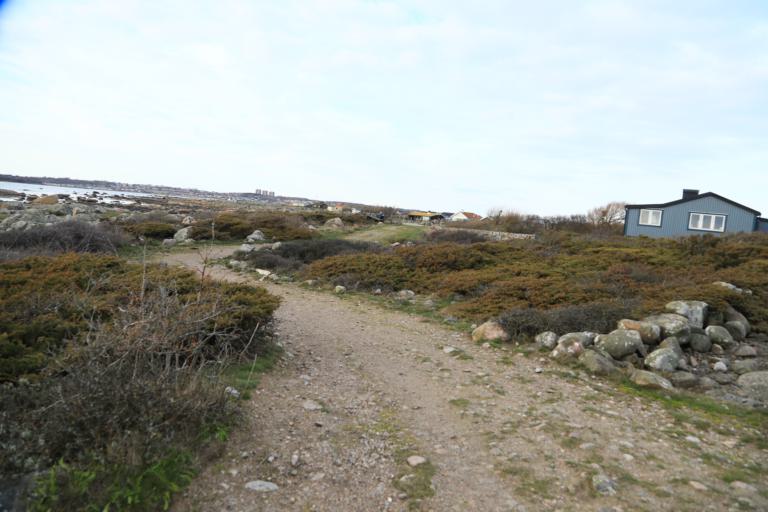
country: SE
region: Halland
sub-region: Varbergs Kommun
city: Traslovslage
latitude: 57.0662
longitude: 12.2518
